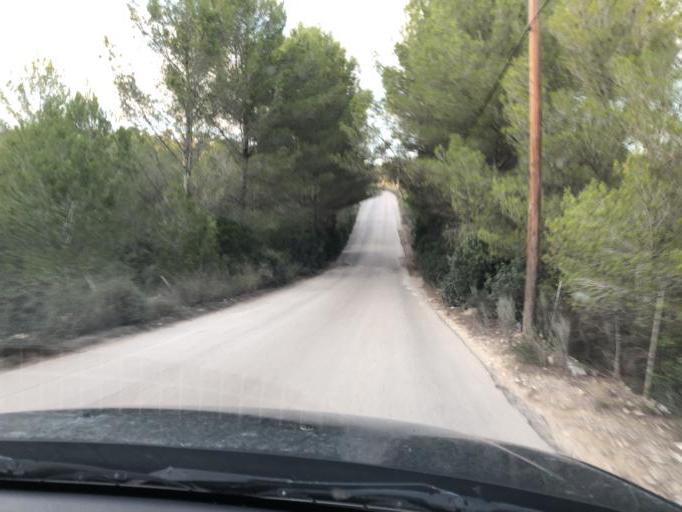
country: ES
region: Balearic Islands
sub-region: Illes Balears
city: Santa Ponsa
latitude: 39.5314
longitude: 2.4810
